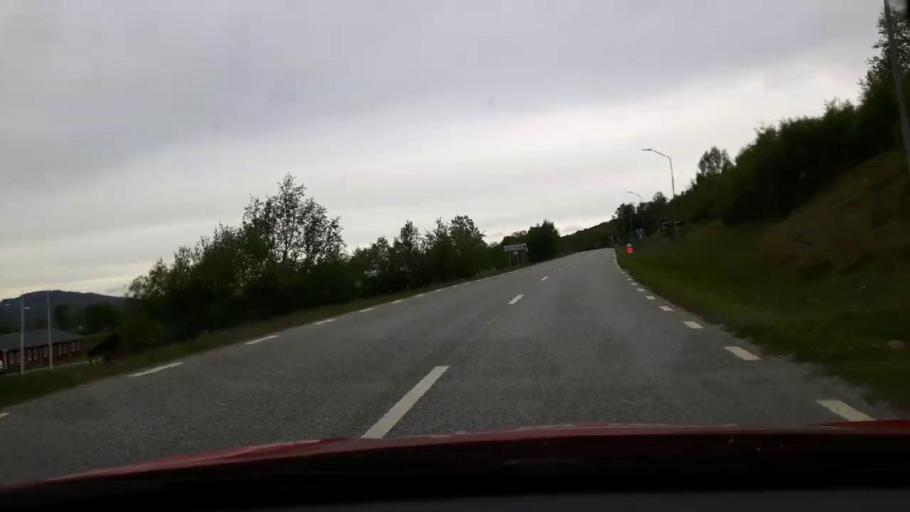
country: NO
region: Sor-Trondelag
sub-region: Tydal
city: Aas
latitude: 62.5949
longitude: 12.1840
